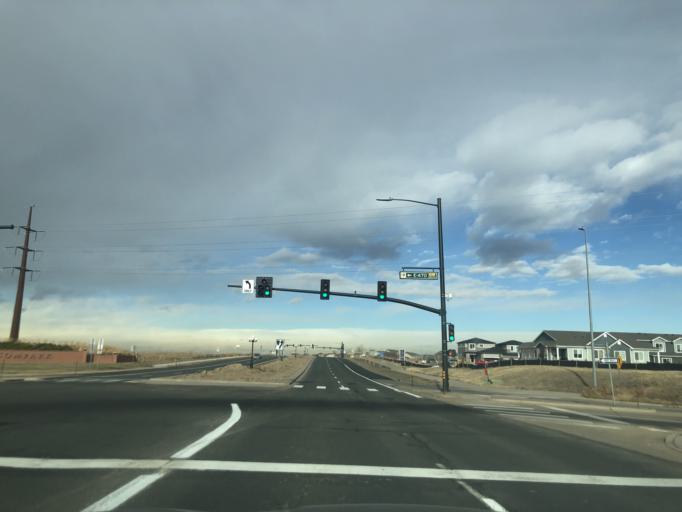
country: US
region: Colorado
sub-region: Douglas County
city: Stonegate
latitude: 39.5533
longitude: -104.8078
